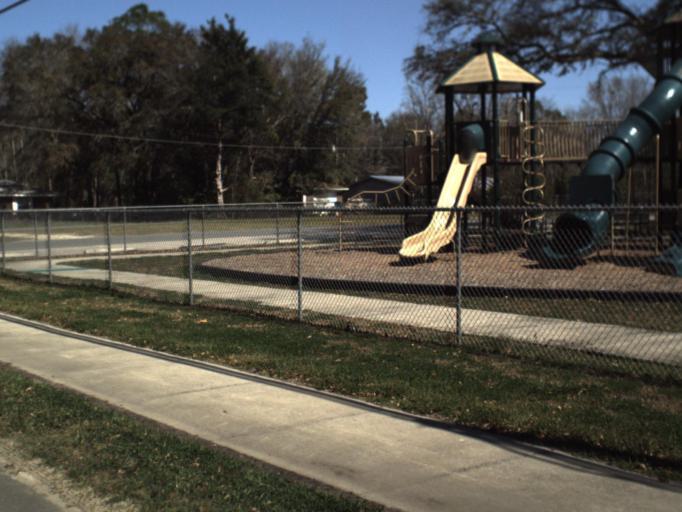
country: US
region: Florida
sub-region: Jackson County
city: Sneads
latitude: 30.7090
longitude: -85.0202
